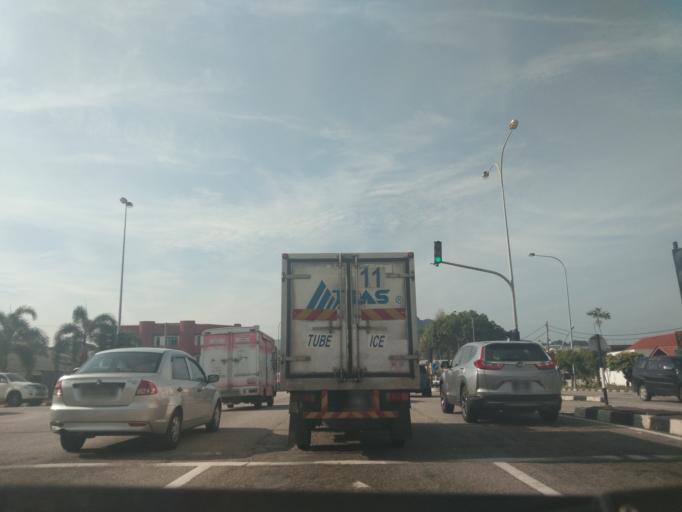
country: MY
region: Perak
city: Ipoh
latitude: 4.5753
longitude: 101.1104
